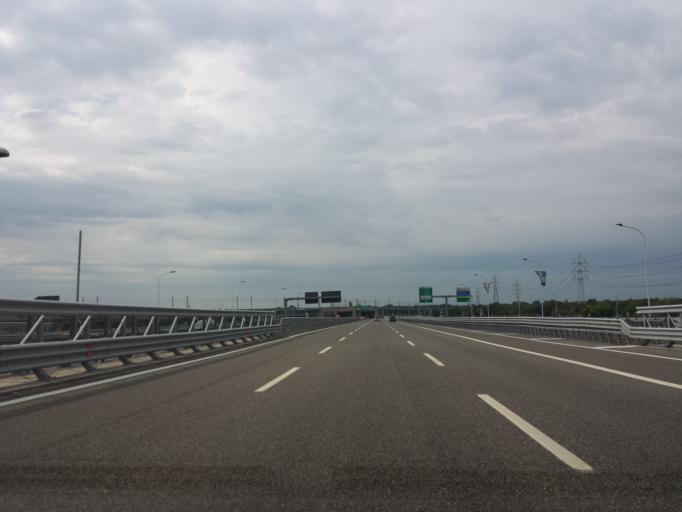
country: IT
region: Lombardy
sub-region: Citta metropolitana di Milano
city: Rho
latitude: 45.5245
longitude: 9.0605
